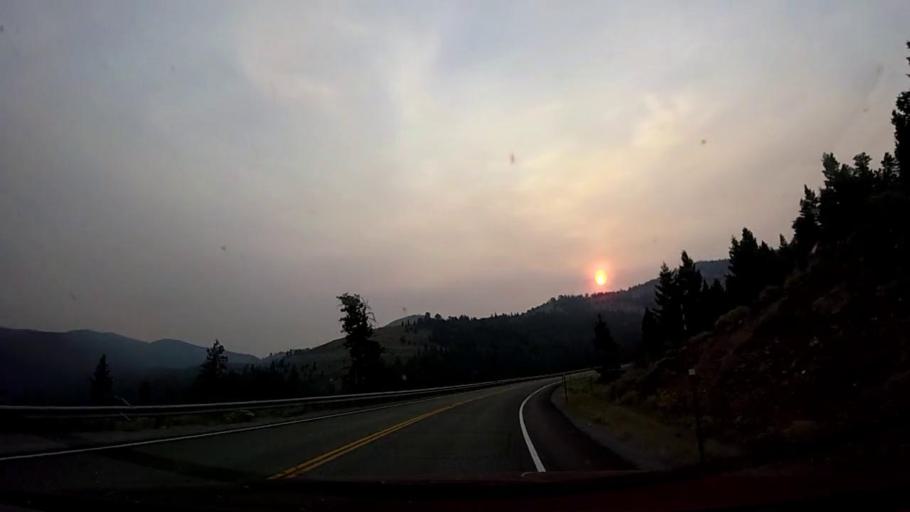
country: US
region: Idaho
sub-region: Blaine County
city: Ketchum
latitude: 43.8853
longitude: -114.6909
